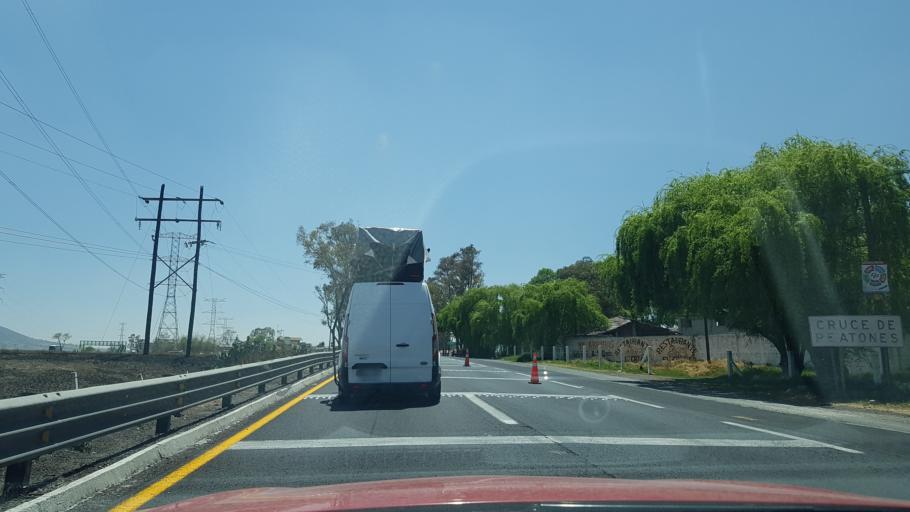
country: MX
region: Mexico
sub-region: Ixtlahuaca
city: Santo Domingo de Guzman
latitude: 19.6002
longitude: -99.7732
